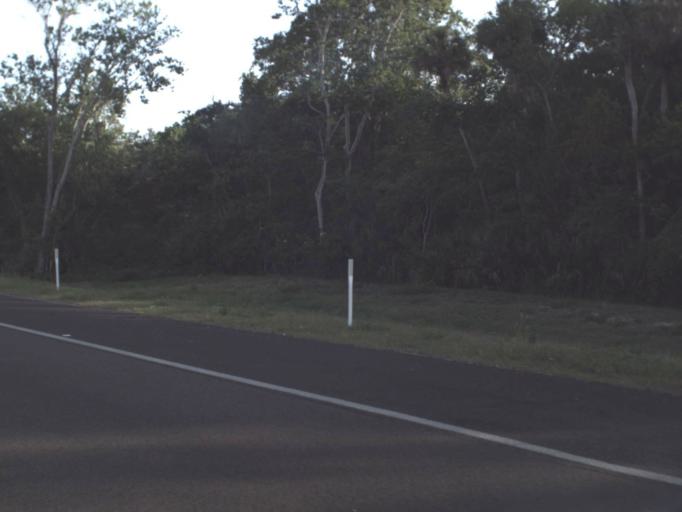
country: US
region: Florida
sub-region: Brevard County
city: Mims
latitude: 28.6610
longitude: -80.8677
